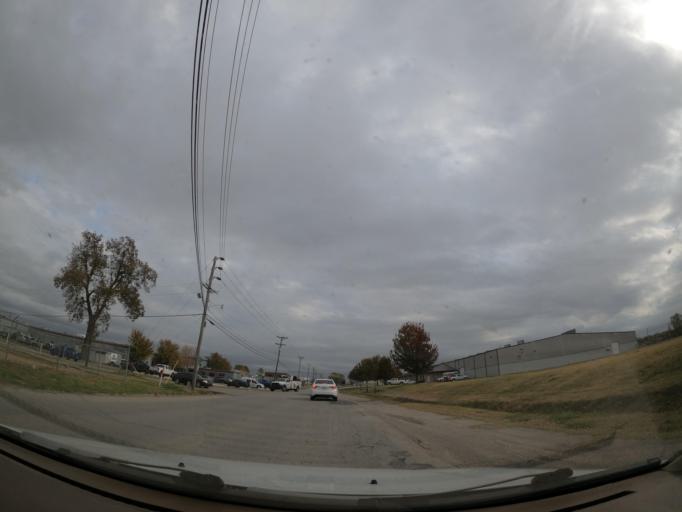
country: US
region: Oklahoma
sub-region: Tulsa County
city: Tulsa
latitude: 36.1043
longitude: -96.0024
